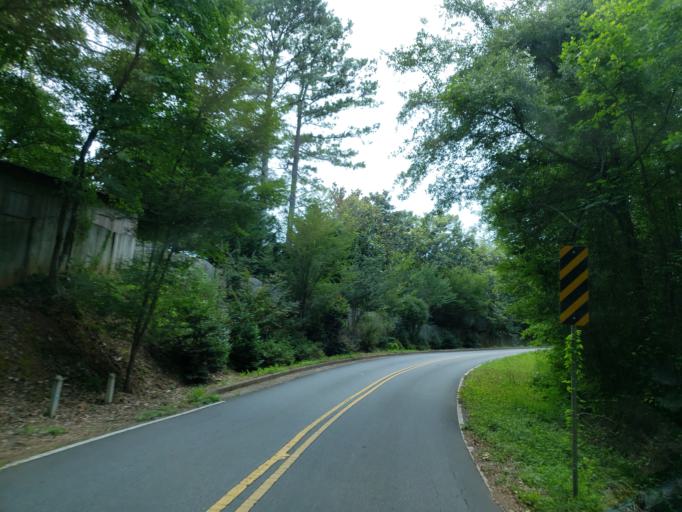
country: US
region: Georgia
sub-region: Cherokee County
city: Holly Springs
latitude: 34.1285
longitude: -84.4519
